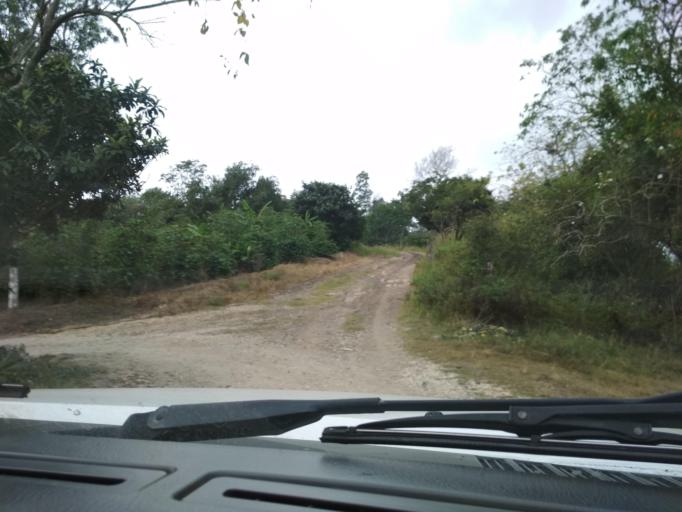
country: MX
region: Veracruz
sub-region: Emiliano Zapata
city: Dos Rios
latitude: 19.5408
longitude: -96.8001
